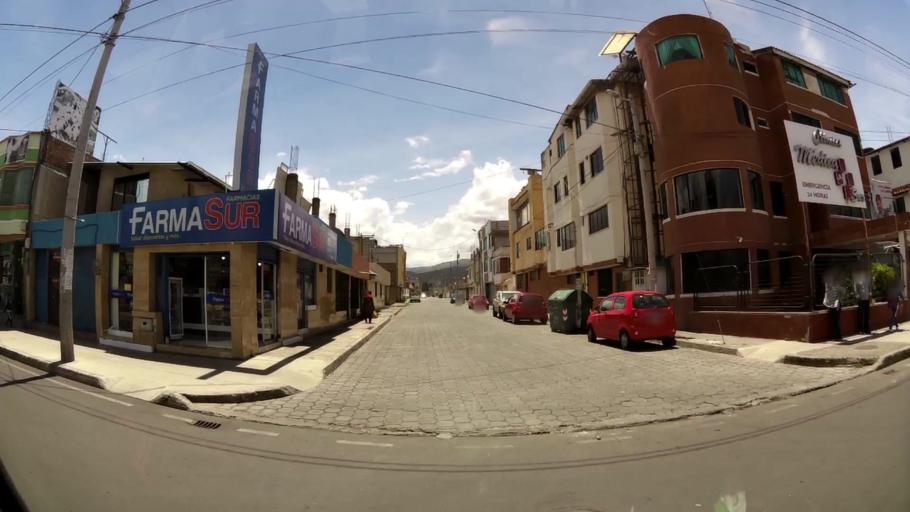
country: EC
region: Chimborazo
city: Riobamba
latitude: -1.6850
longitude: -78.6352
